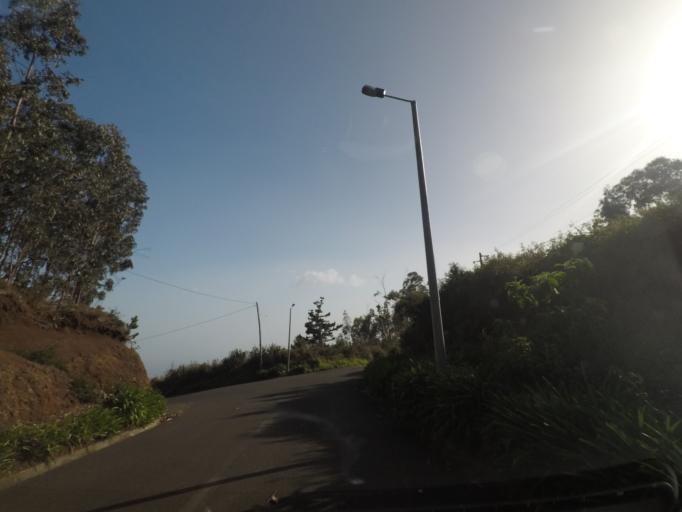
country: PT
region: Madeira
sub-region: Ribeira Brava
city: Campanario
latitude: 32.6819
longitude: -17.0083
